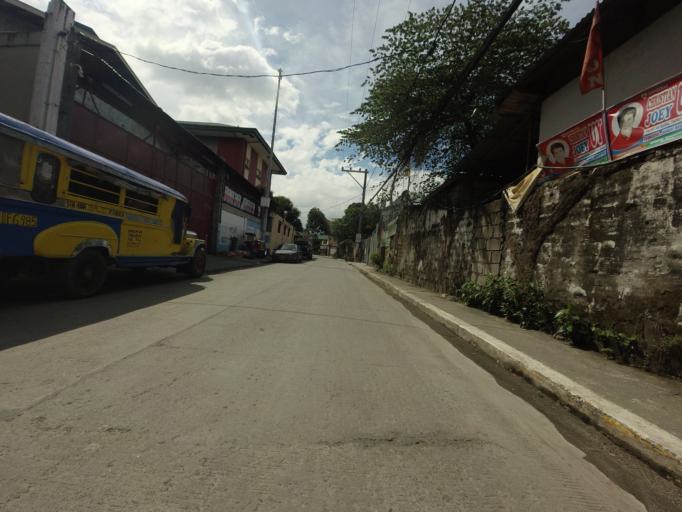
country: PH
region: Metro Manila
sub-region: San Juan
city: San Juan
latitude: 14.5836
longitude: 121.0141
